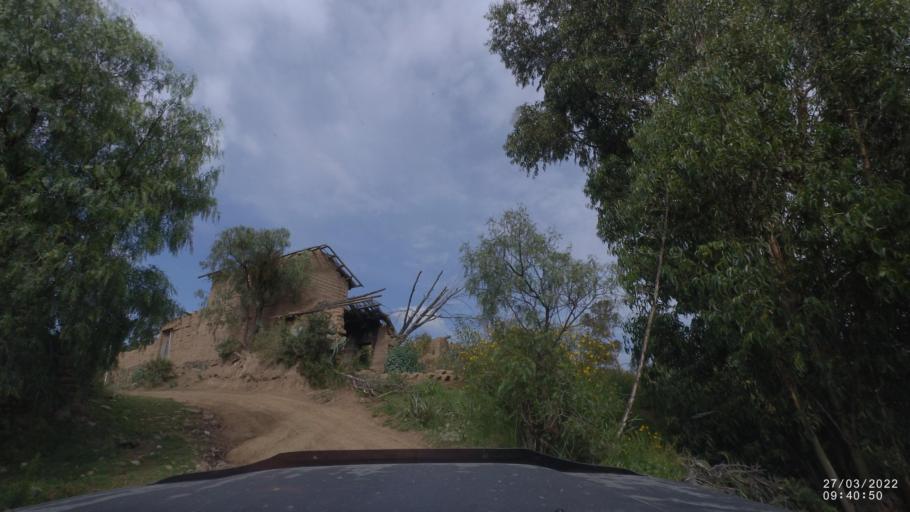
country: BO
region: Cochabamba
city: Cliza
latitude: -17.7512
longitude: -65.8995
